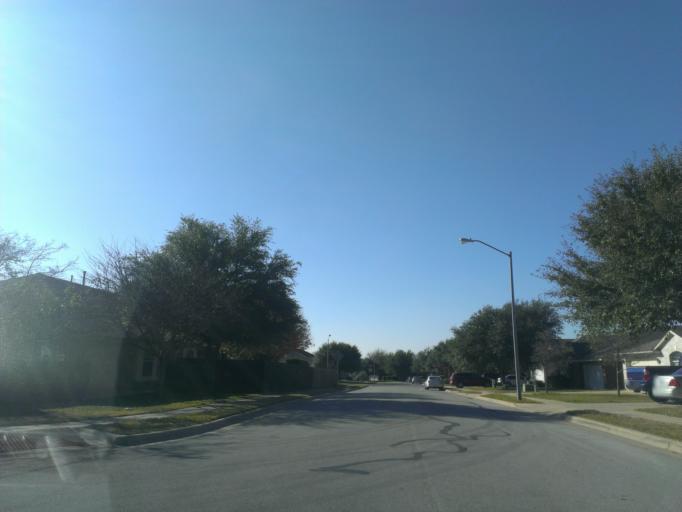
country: US
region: Texas
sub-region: Williamson County
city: Round Rock
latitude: 30.5356
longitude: -97.6228
